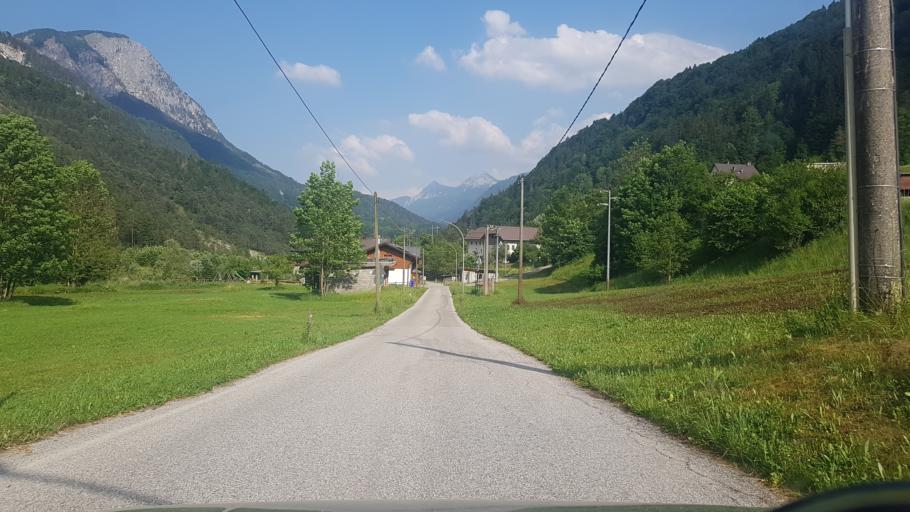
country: IT
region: Friuli Venezia Giulia
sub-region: Provincia di Udine
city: Pontebba
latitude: 46.5214
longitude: 13.2713
